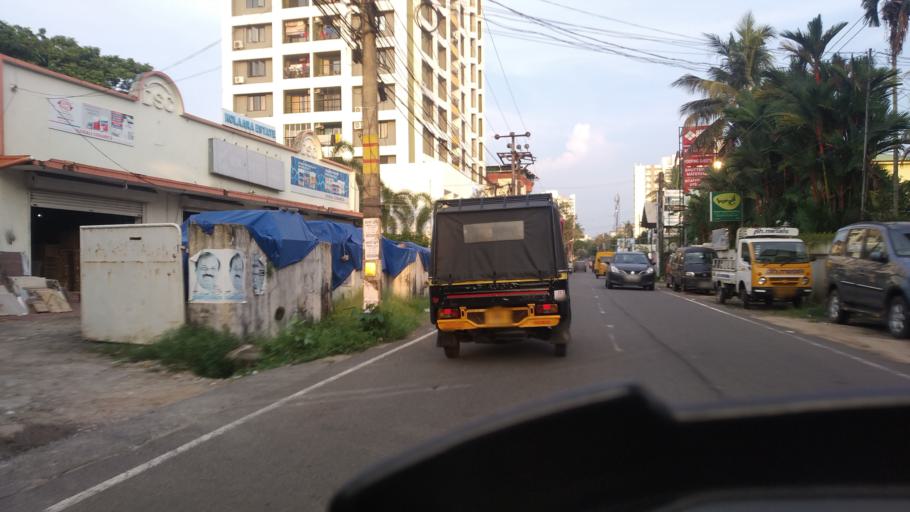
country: IN
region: Kerala
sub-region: Ernakulam
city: Elur
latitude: 10.0194
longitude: 76.2935
